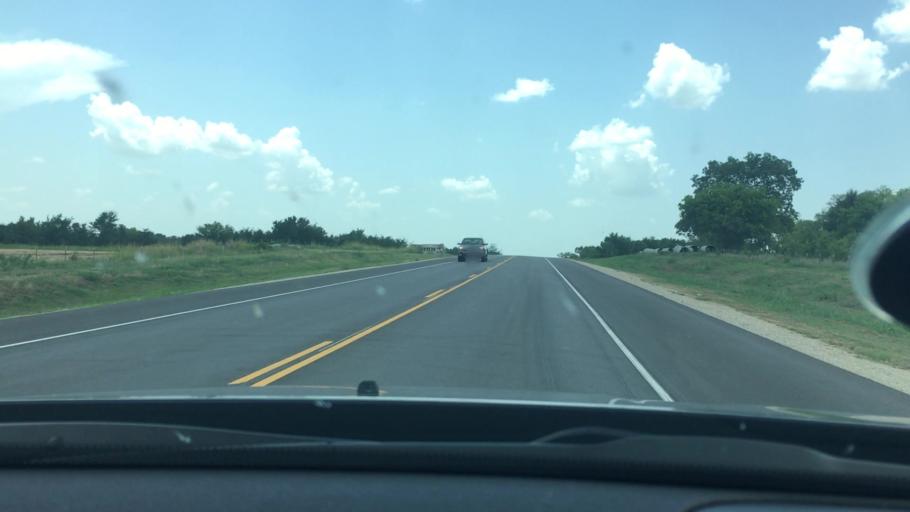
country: US
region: Oklahoma
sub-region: Johnston County
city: Tishomingo
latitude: 34.3342
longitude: -96.6519
